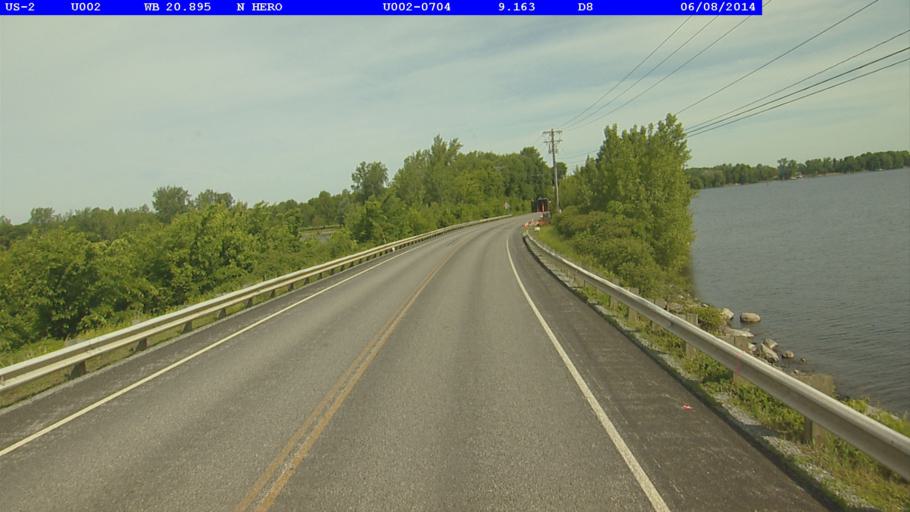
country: US
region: Vermont
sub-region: Grand Isle County
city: North Hero
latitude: 44.7682
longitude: -73.2923
